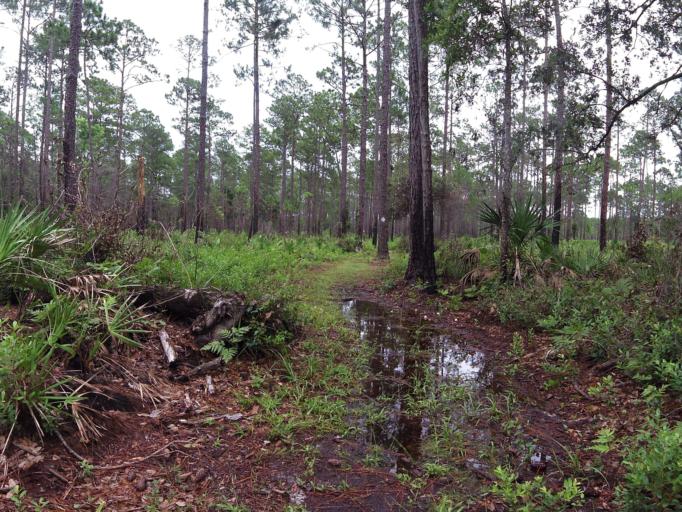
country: US
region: Florida
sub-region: Clay County
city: Green Cove Springs
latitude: 29.9704
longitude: -81.6331
